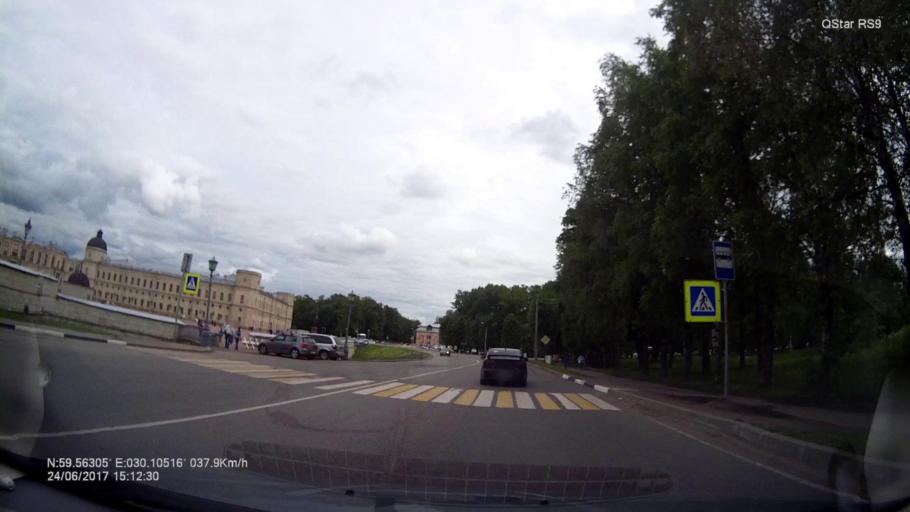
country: RU
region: Leningrad
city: Gatchina
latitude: 59.5630
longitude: 30.1053
